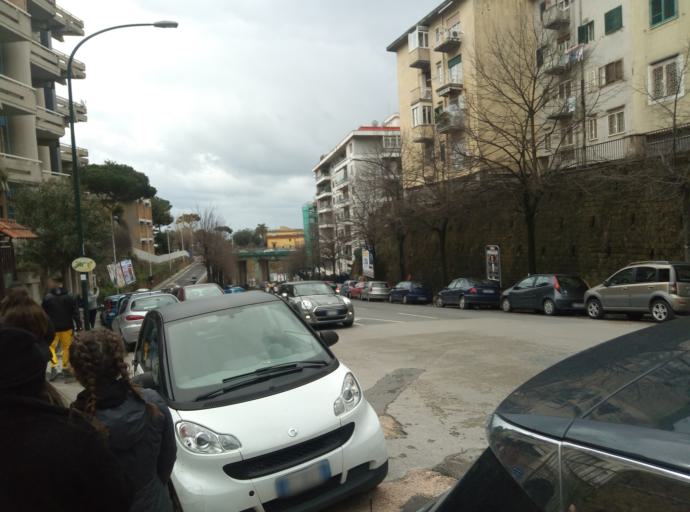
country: IT
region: Campania
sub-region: Provincia di Napoli
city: Napoli
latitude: 40.8603
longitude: 14.2253
